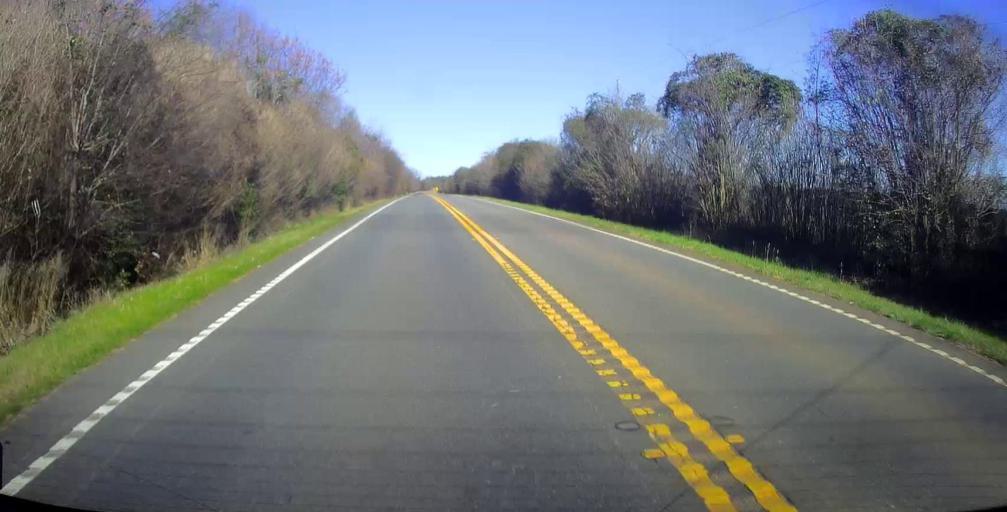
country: US
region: Georgia
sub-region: Macon County
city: Marshallville
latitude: 32.4452
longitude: -83.9856
